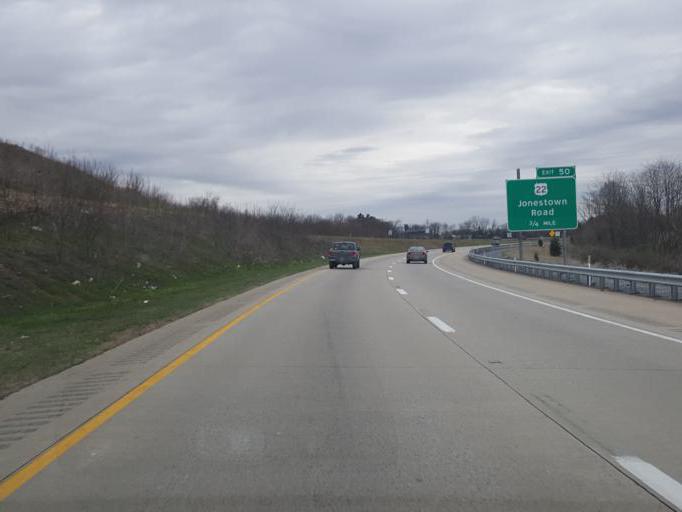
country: US
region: Pennsylvania
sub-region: Dauphin County
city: Progress
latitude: 40.3066
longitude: -76.8364
